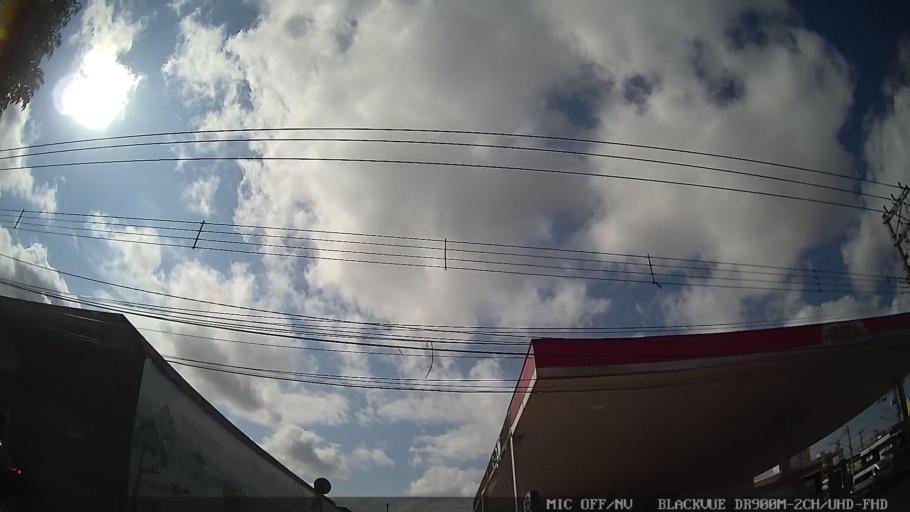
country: BR
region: Sao Paulo
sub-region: Guarulhos
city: Guarulhos
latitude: -23.5062
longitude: -46.4767
